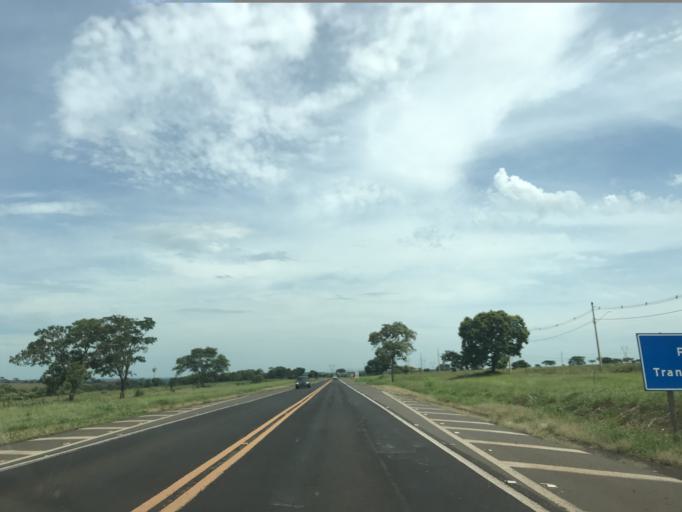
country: BR
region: Sao Paulo
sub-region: Nova Granada
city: Nova Granada
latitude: -20.3483
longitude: -49.2149
